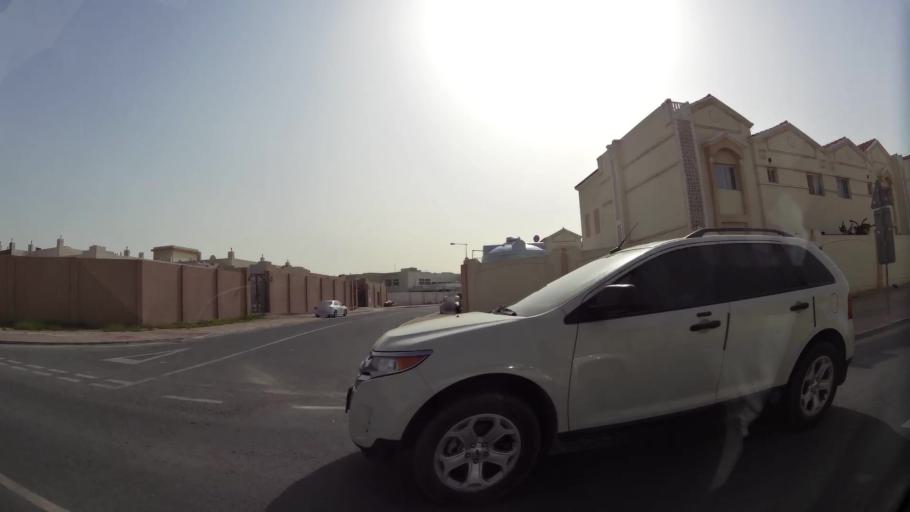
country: QA
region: Baladiyat ar Rayyan
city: Ar Rayyan
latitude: 25.2408
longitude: 51.4399
